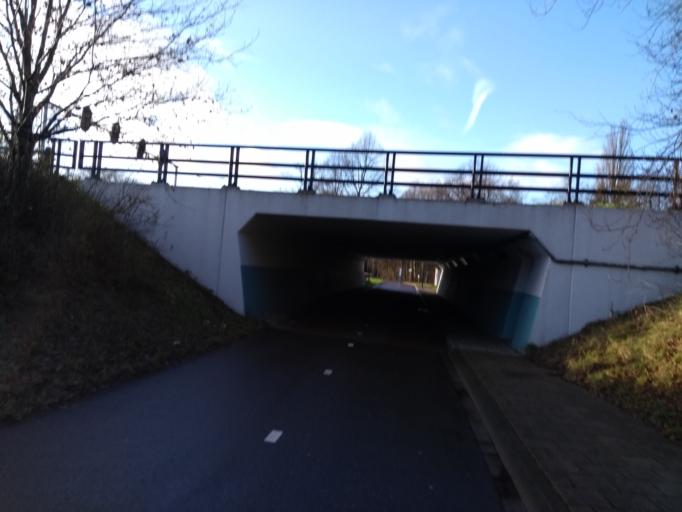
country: NL
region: Overijssel
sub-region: Gemeente Wierden
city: Wierden
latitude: 52.3562
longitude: 6.6255
